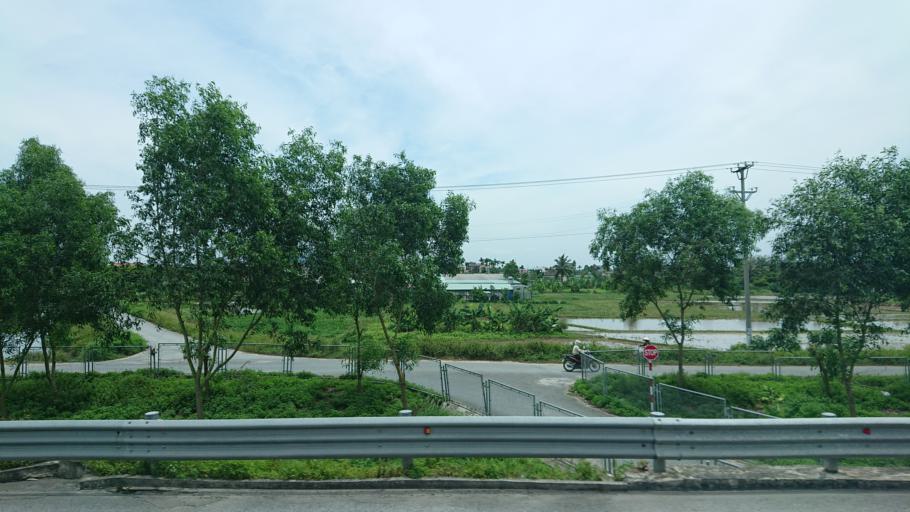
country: VN
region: Hai Phong
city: Nui Doi
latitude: 20.7688
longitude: 106.6319
